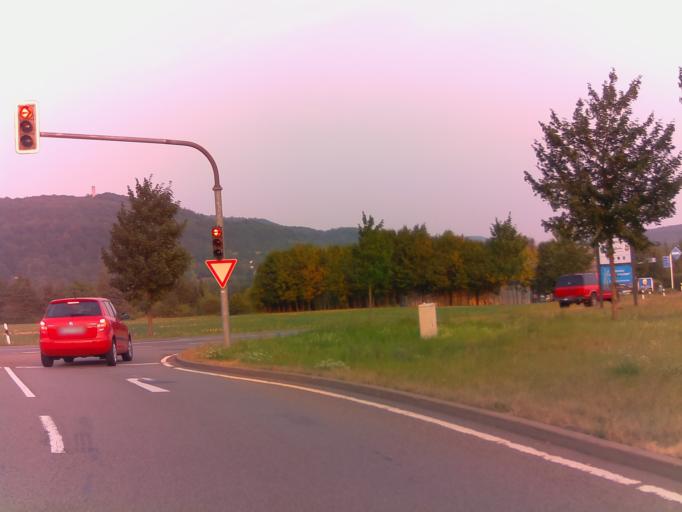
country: DE
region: Thuringia
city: Bad Berka
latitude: 50.9057
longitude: 11.2762
